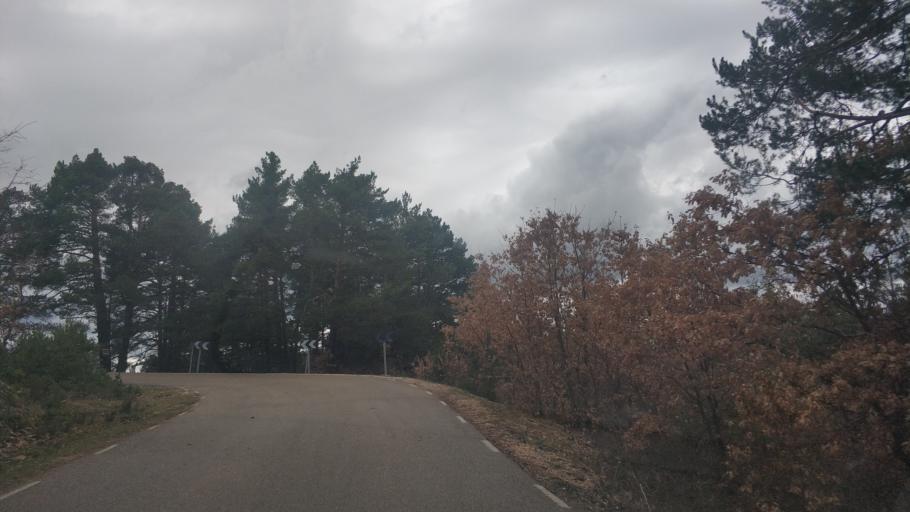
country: ES
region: Castille and Leon
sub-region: Provincia de Burgos
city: Canicosa de la Sierra
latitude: 41.9312
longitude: -3.0386
